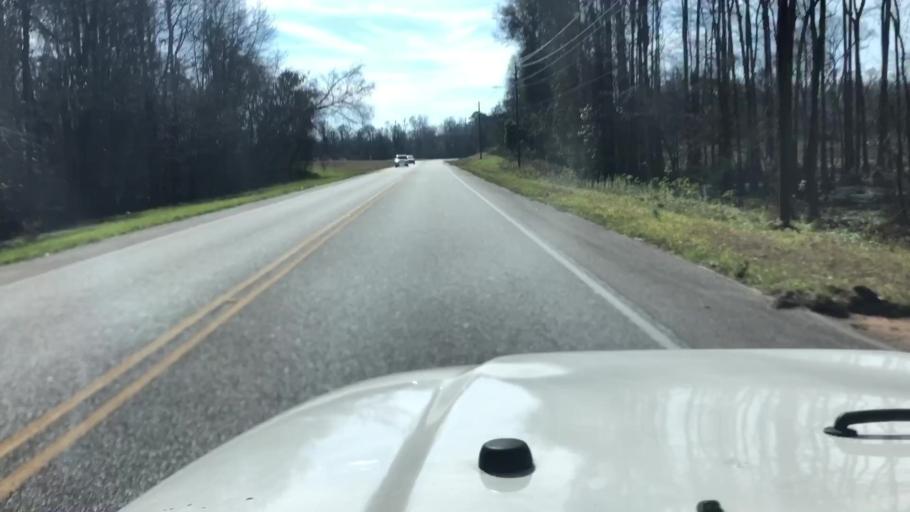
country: US
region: Alabama
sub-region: Elmore County
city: Blue Ridge
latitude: 32.4007
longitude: -86.1664
